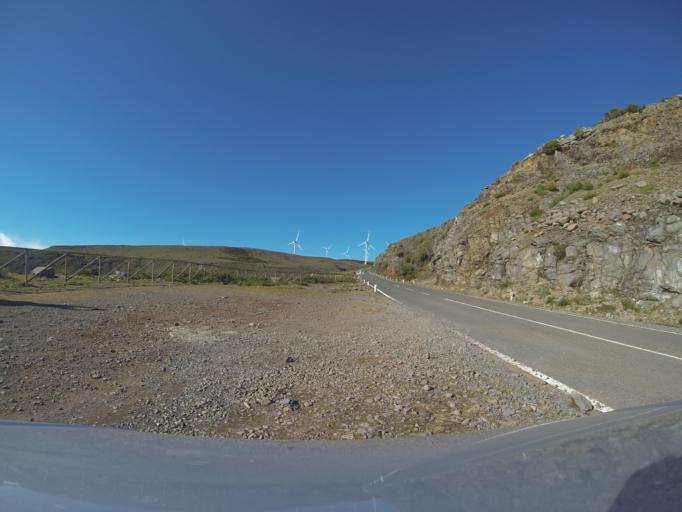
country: PT
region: Madeira
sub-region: Sao Vicente
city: Sao Vicente
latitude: 32.7368
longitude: -17.0610
